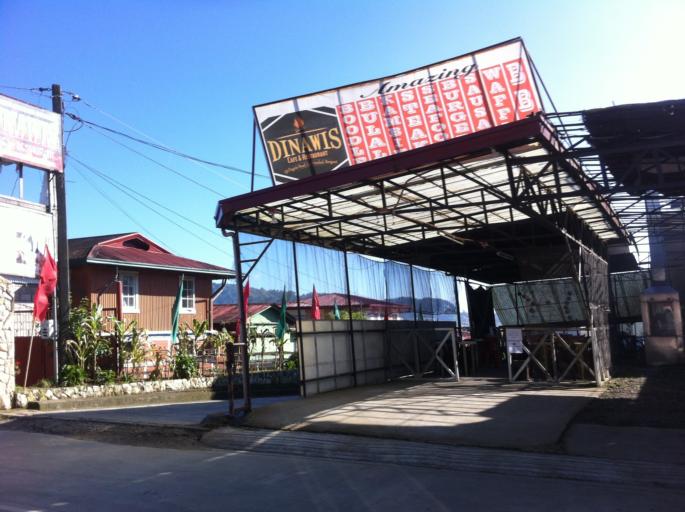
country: PH
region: Cordillera
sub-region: Province of Benguet
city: La Trinidad
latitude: 16.4469
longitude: 120.5771
